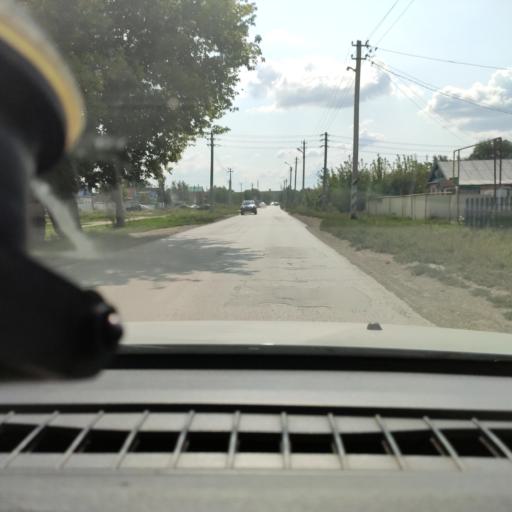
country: RU
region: Samara
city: Chapayevsk
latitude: 52.9969
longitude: 49.7160
